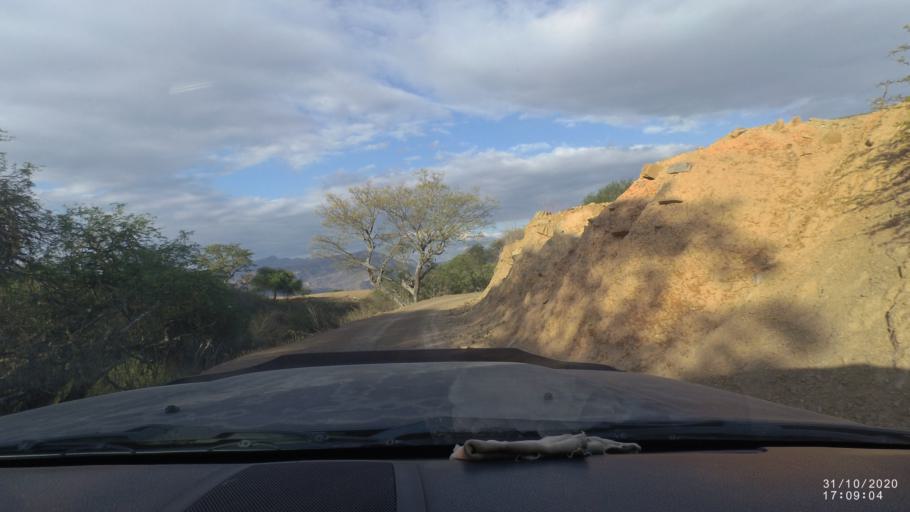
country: BO
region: Chuquisaca
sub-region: Provincia Zudanez
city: Mojocoya
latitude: -18.5485
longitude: -64.5389
